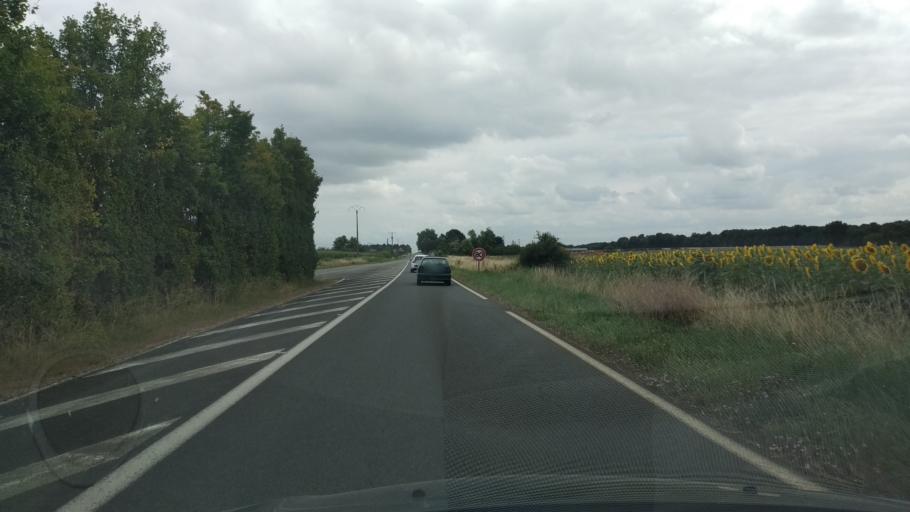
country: FR
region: Poitou-Charentes
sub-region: Departement de la Vienne
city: La Villedieu-du-Clain
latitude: 46.4147
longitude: 0.3859
